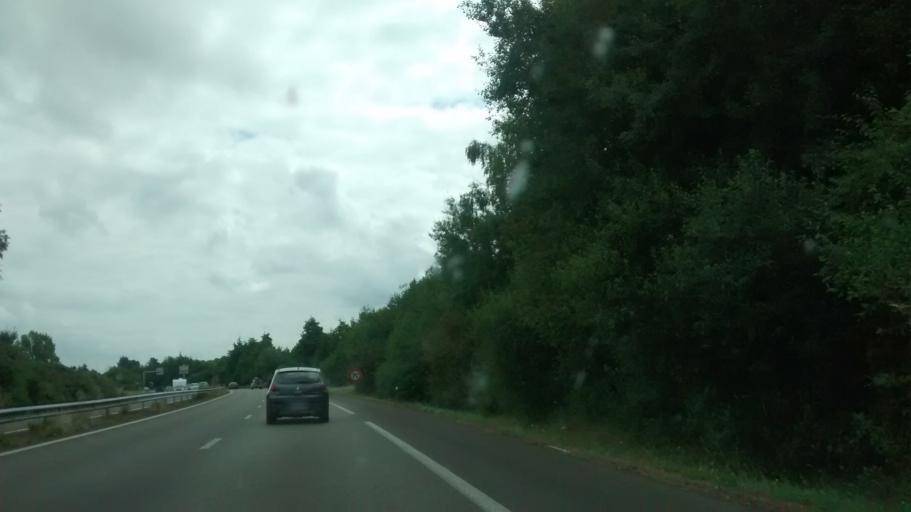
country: FR
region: Brittany
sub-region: Departement d'Ille-et-Vilaine
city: Hede-Bazouges
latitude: 48.2850
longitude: -1.8020
